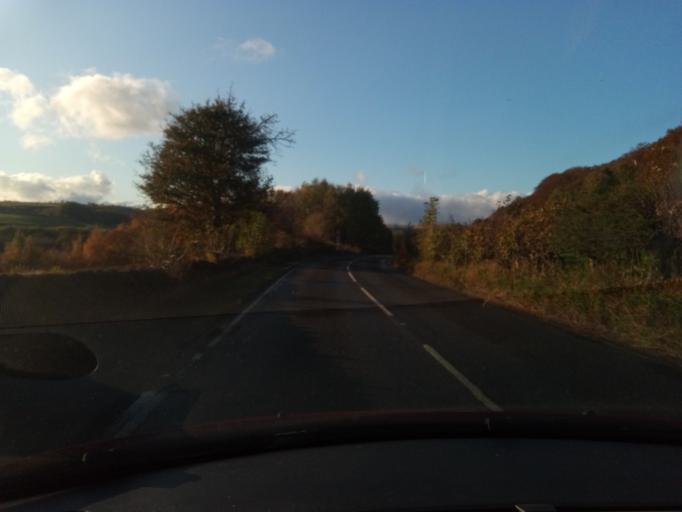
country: GB
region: England
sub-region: County Durham
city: Stanhope
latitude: 54.7340
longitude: -1.9813
